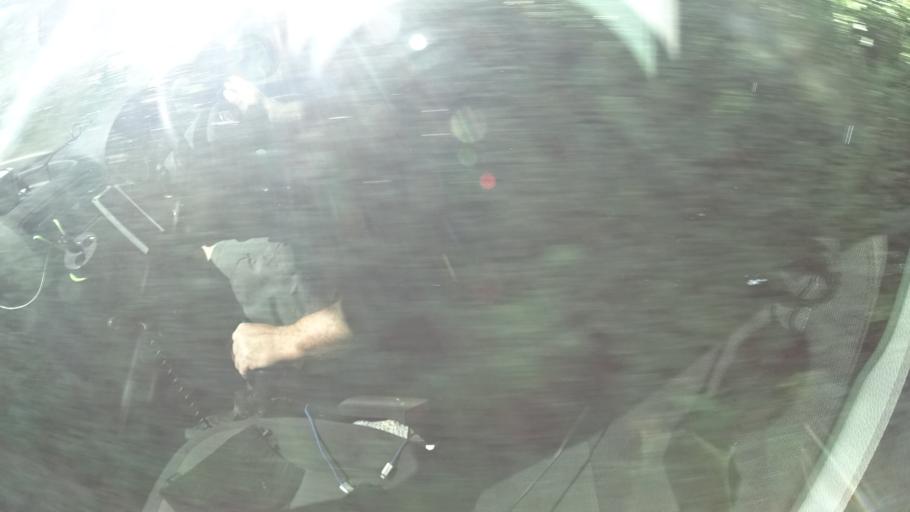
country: DE
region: Bavaria
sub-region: Regierungsbezirk Unterfranken
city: Gadheim
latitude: 49.8490
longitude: 9.9060
